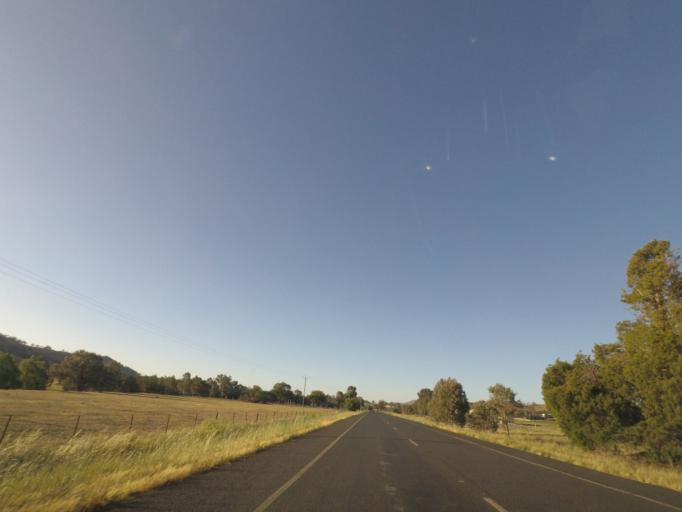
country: AU
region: New South Wales
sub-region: Gundagai
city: Gundagai
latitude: -34.9348
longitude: 148.1671
